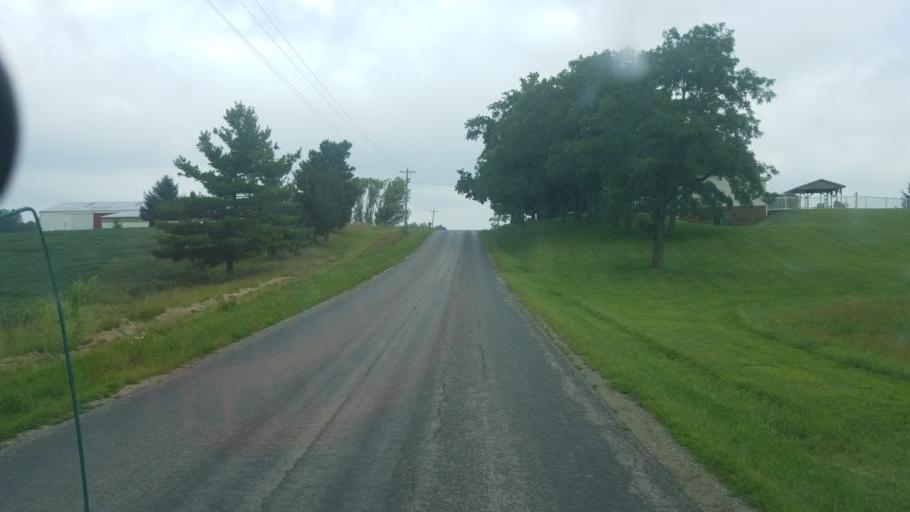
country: US
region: Ohio
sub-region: Huron County
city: Greenwich
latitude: 40.9771
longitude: -82.4714
